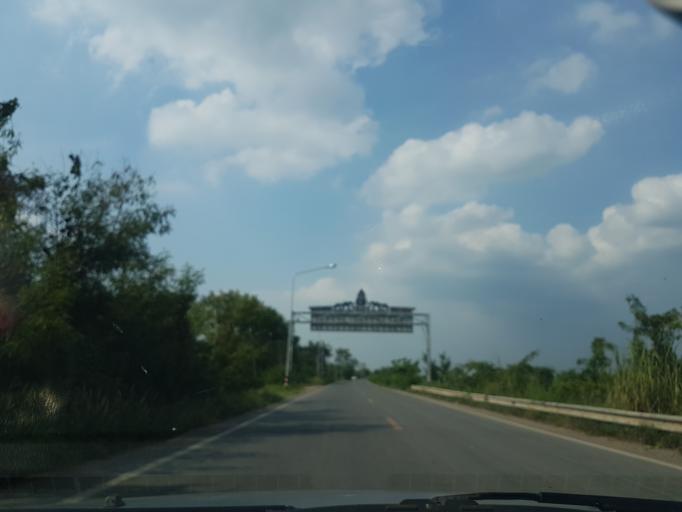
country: TH
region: Phra Nakhon Si Ayutthaya
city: Phachi
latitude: 14.4014
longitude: 100.7898
